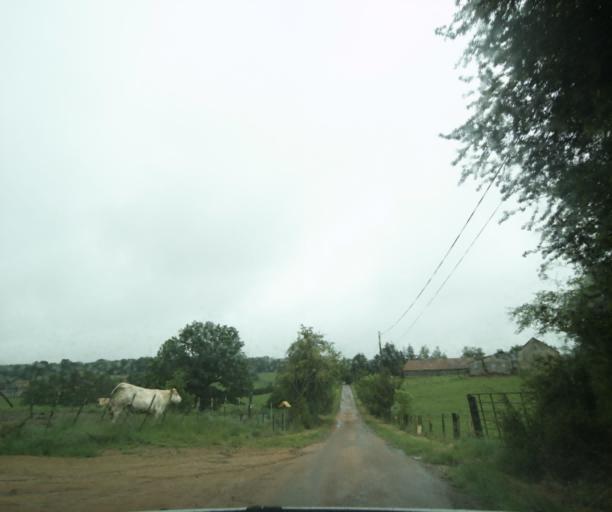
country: FR
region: Bourgogne
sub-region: Departement de Saone-et-Loire
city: Paray-le-Monial
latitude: 46.4715
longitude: 4.1953
